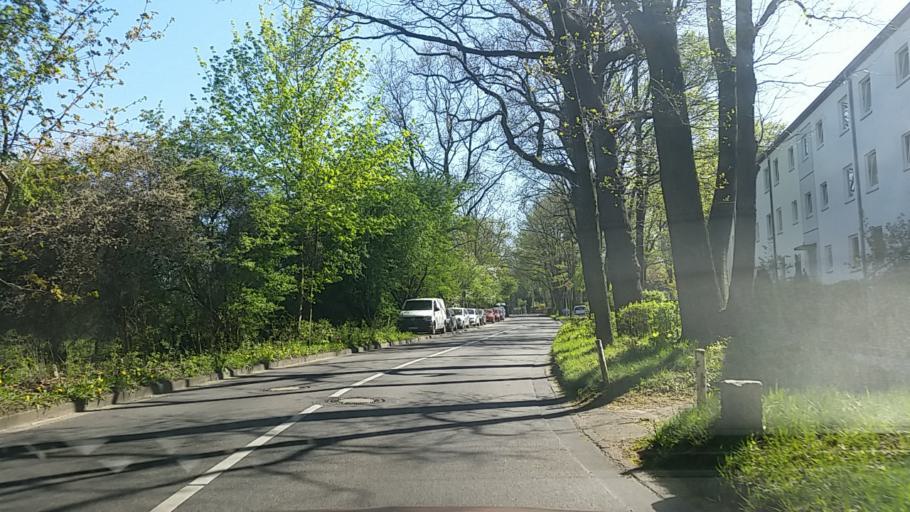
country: DE
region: Schleswig-Holstein
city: Halstenbek
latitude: 53.5787
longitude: 9.8338
